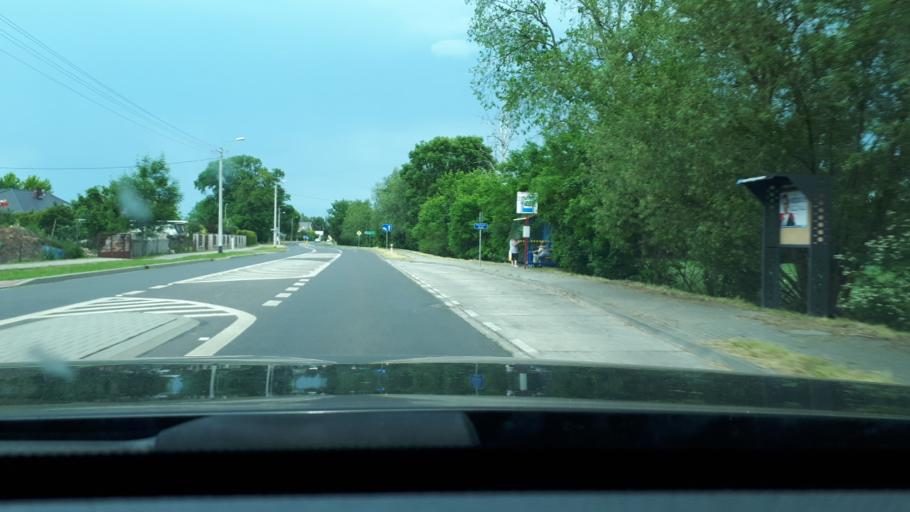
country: PL
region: Masovian Voivodeship
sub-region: Powiat warszawski zachodni
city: Leszno
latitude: 52.2582
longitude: 20.5407
